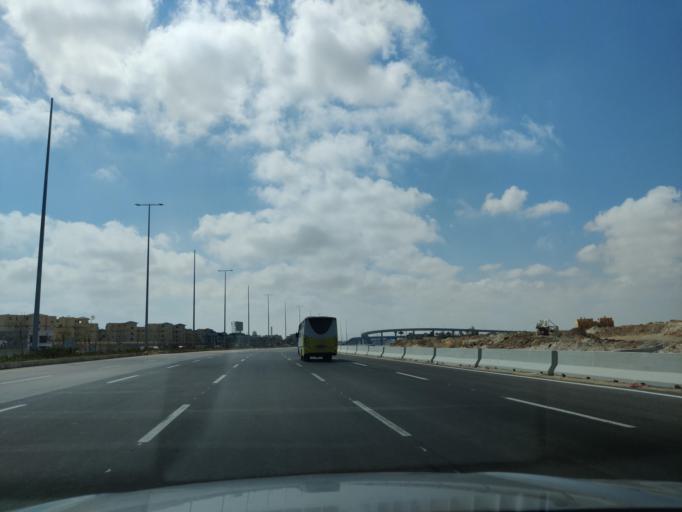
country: EG
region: Muhafazat Matruh
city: Al `Alamayn
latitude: 30.9570
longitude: 28.7649
